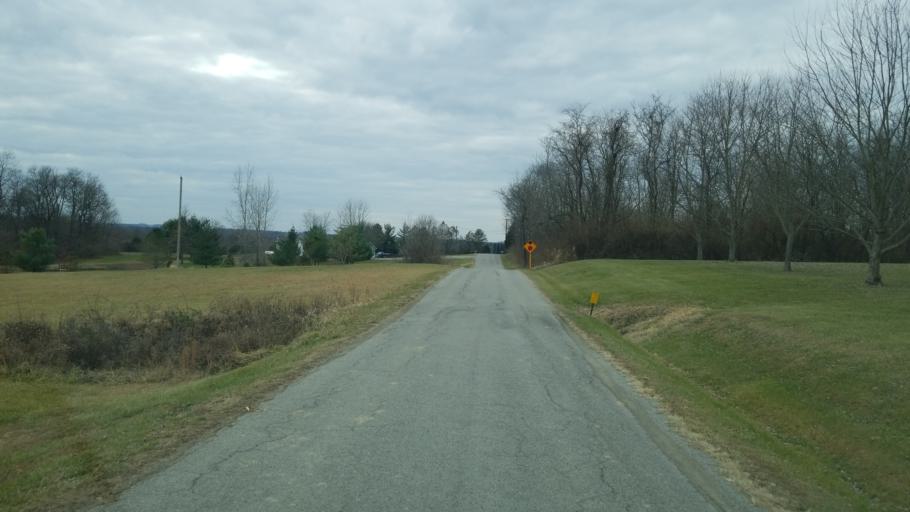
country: US
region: Ohio
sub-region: Highland County
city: Greenfield
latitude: 39.2978
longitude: -83.3623
